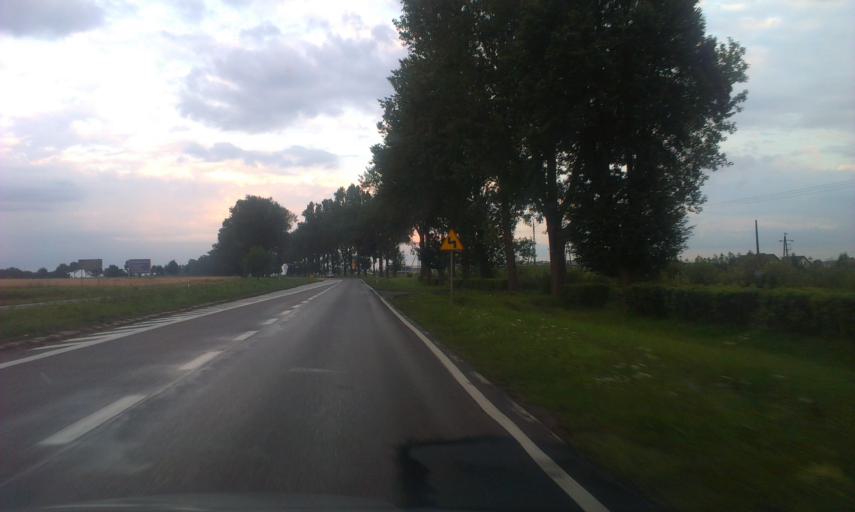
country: PL
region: West Pomeranian Voivodeship
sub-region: Koszalin
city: Koszalin
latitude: 54.1612
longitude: 16.2239
